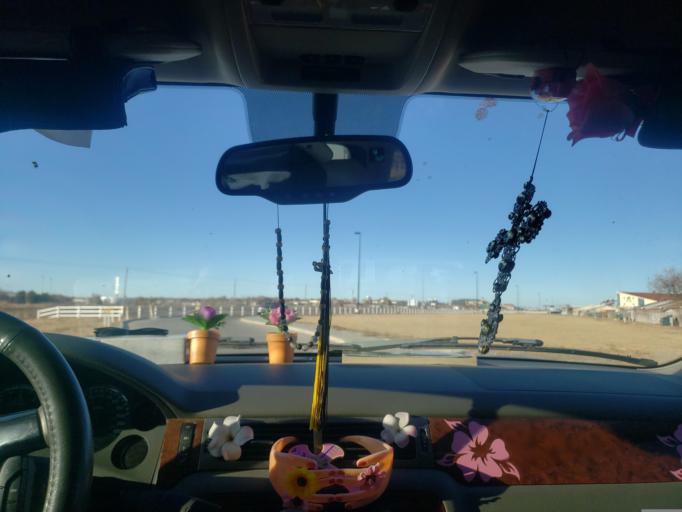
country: US
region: Kansas
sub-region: Finney County
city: Garden City
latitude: 37.9684
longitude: -100.8383
